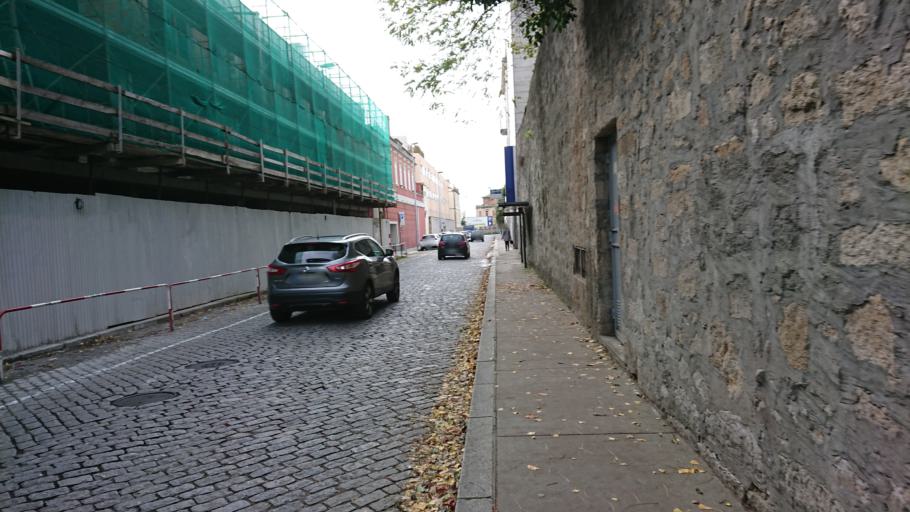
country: PT
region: Porto
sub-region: Porto
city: Porto
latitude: 41.1571
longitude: -8.6250
